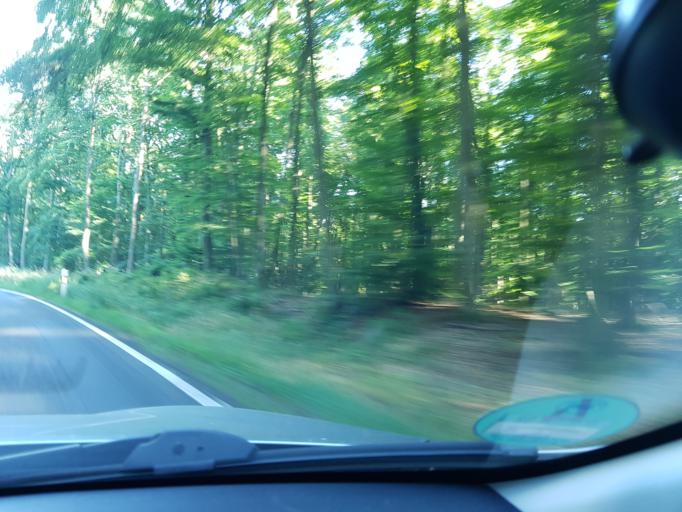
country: DE
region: Rheinland-Pfalz
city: Arzbach
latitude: 50.4006
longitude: 7.7799
